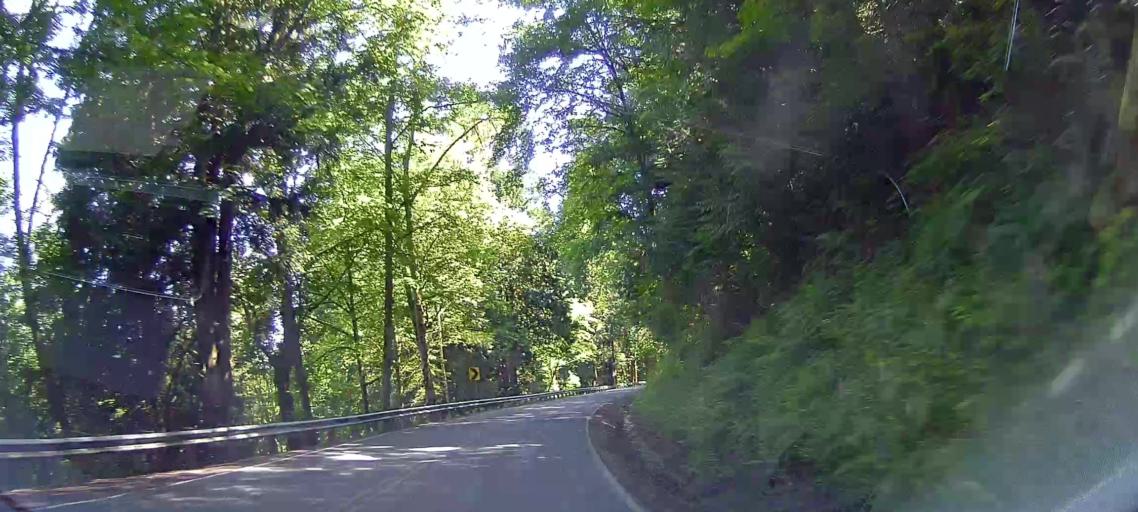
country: US
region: Washington
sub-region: Skagit County
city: Burlington
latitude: 48.5502
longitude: -122.3097
